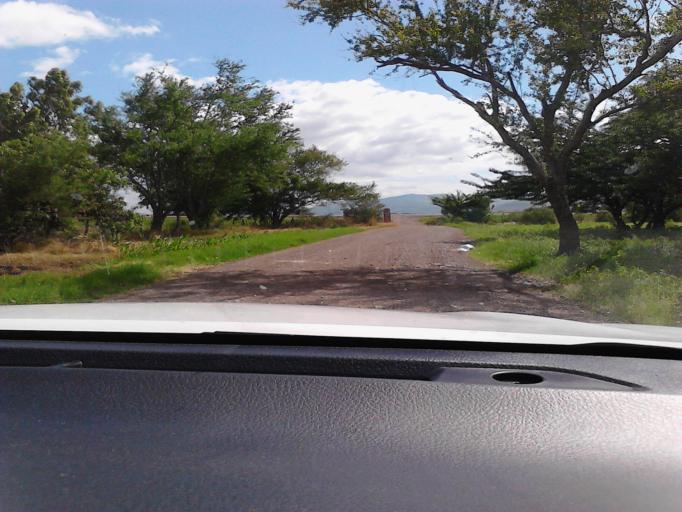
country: NI
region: Matagalpa
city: Ciudad Dario
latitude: 12.8928
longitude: -86.1554
